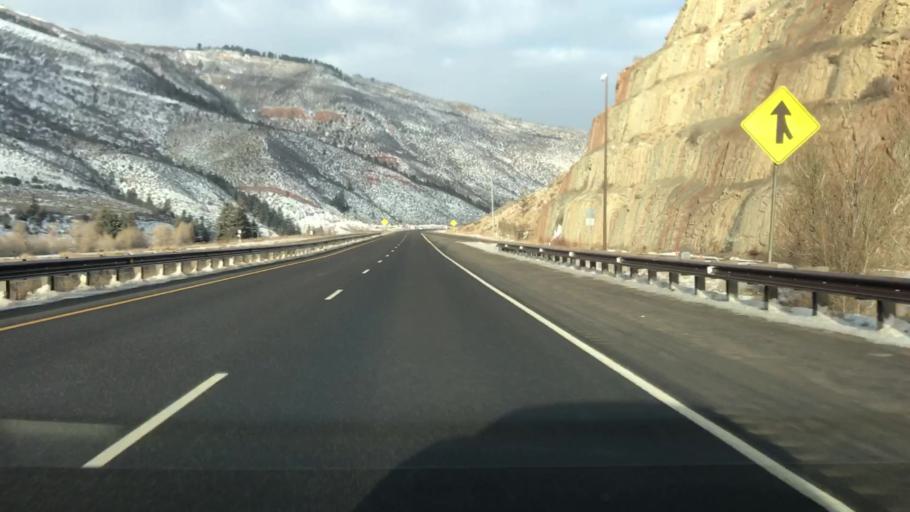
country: US
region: Colorado
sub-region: Eagle County
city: Edwards
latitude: 39.6577
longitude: -106.6329
